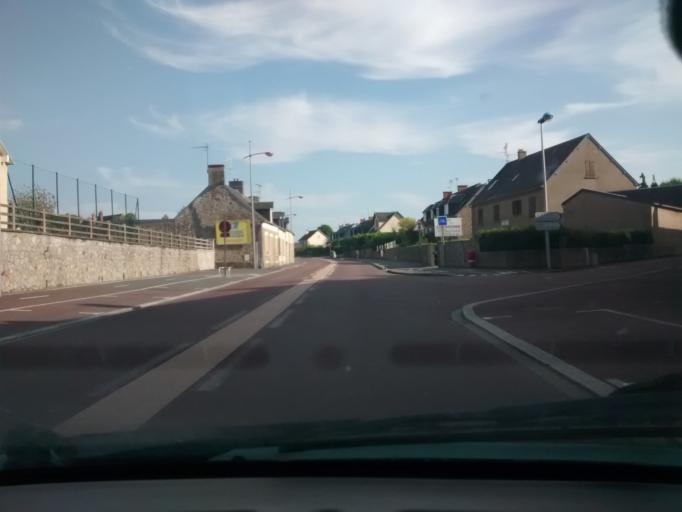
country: FR
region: Lower Normandy
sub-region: Departement de la Manche
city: Lessay
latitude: 49.2165
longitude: -1.5313
